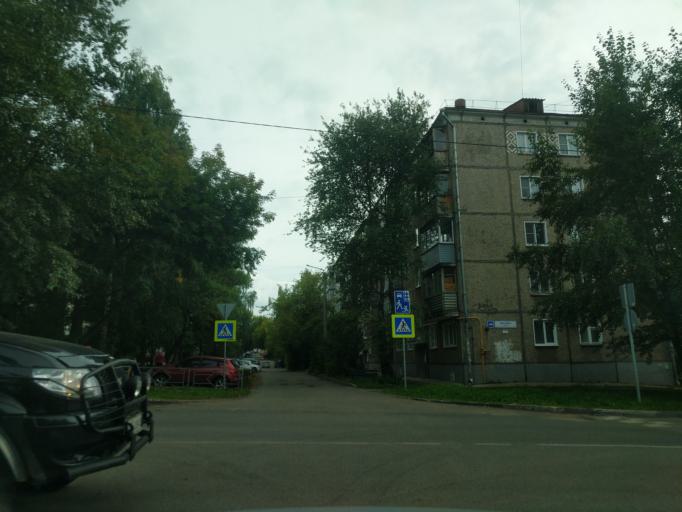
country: RU
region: Kirov
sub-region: Kirovo-Chepetskiy Rayon
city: Kirov
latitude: 58.5958
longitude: 49.6451
